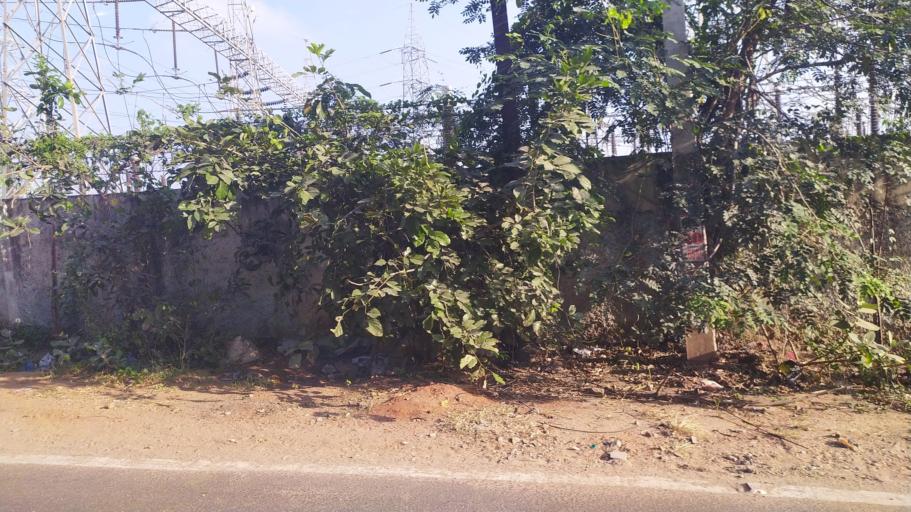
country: IN
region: Telangana
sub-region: Hyderabad
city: Hyderabad
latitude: 17.3271
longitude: 78.4231
